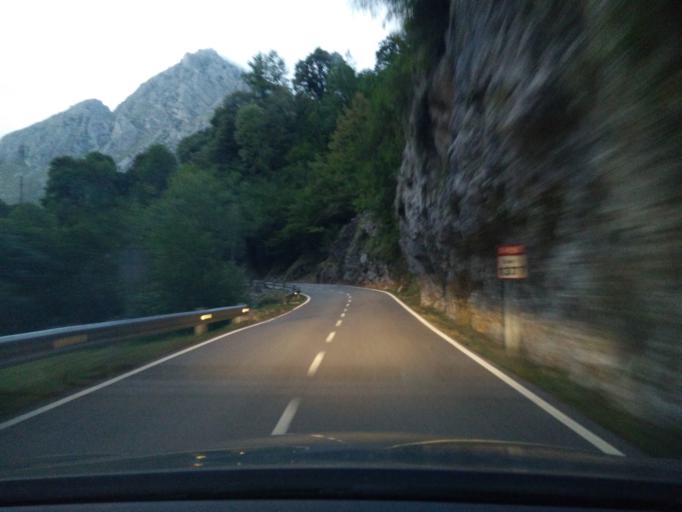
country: ES
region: Asturias
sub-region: Province of Asturias
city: Amieva
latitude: 43.2296
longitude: -5.0920
